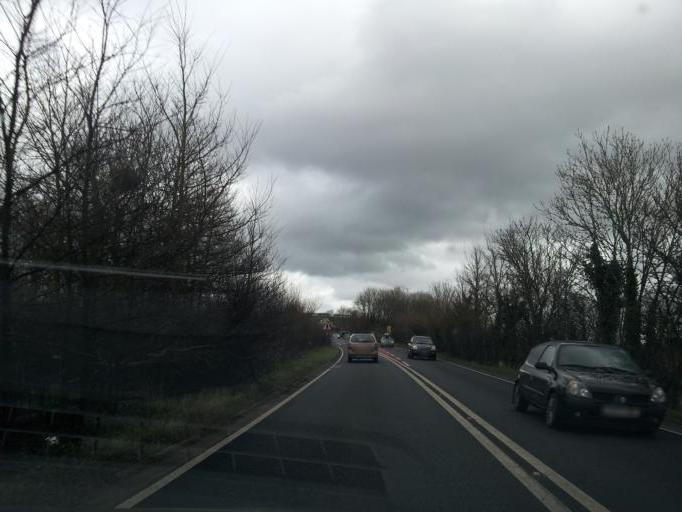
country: GB
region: England
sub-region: Somerset
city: Ilchester
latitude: 51.0214
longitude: -2.6235
